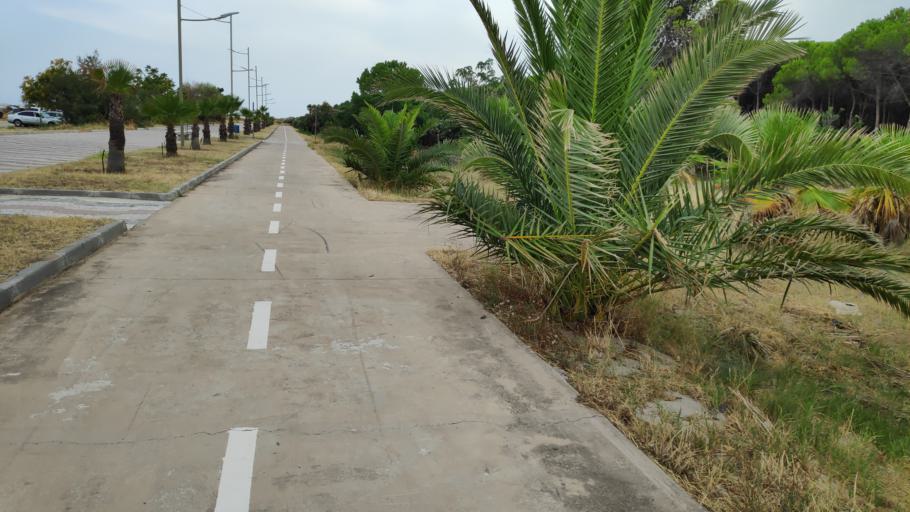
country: IT
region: Calabria
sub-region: Provincia di Catanzaro
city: Soverato Marina
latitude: 38.6829
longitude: 16.5571
